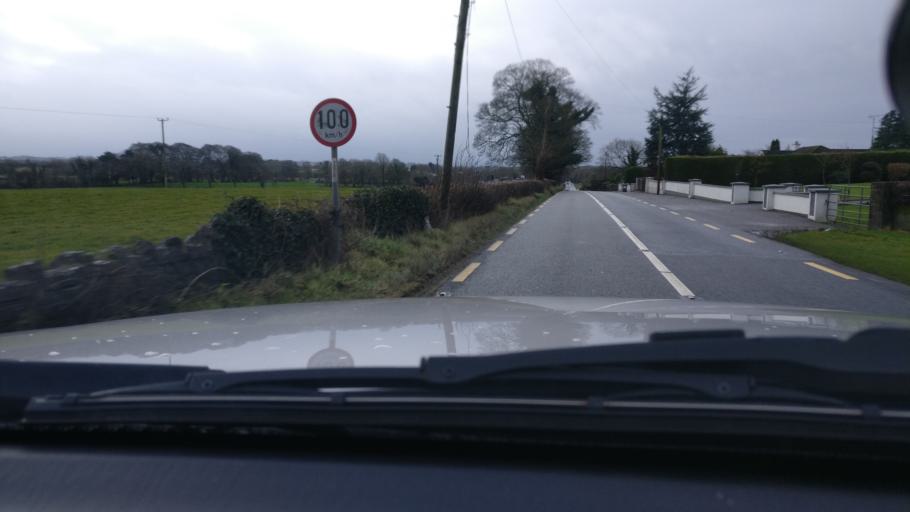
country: IE
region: Leinster
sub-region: An Longfort
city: Ballymahon
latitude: 53.5435
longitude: -7.7852
